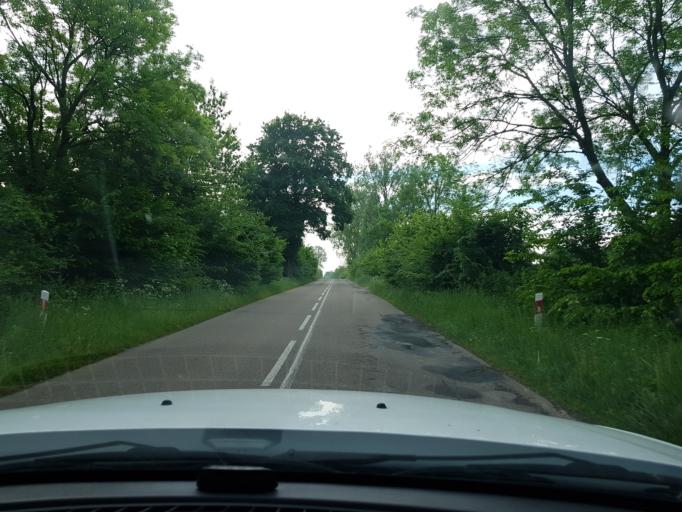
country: PL
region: West Pomeranian Voivodeship
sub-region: Powiat stargardzki
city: Chociwel
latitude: 53.4670
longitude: 15.3621
